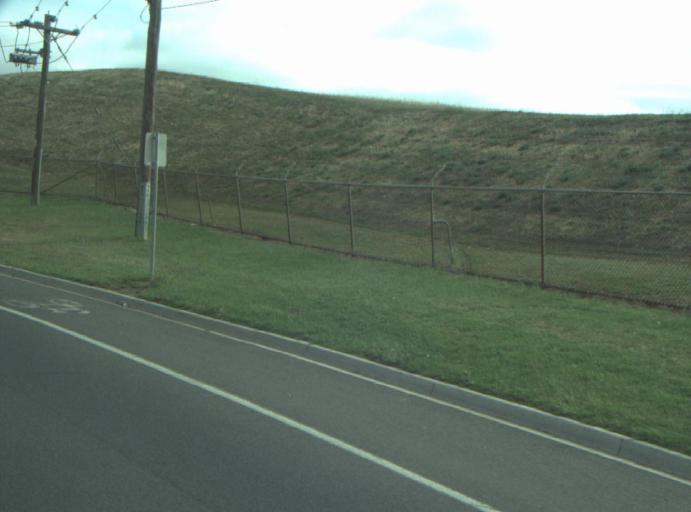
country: AU
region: Victoria
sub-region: Greater Geelong
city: Wandana Heights
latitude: -38.1573
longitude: 144.3119
